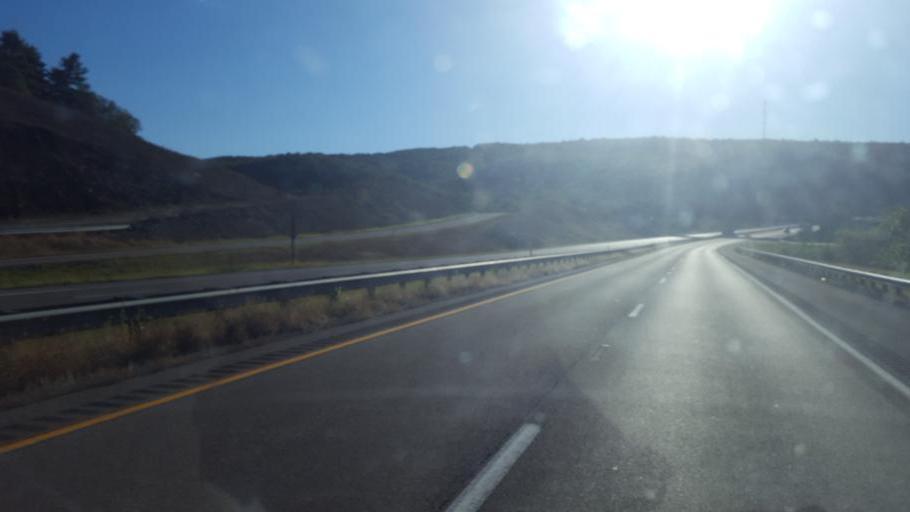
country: US
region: West Virginia
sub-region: Morgan County
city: Berkeley Springs
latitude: 39.6771
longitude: -78.4616
